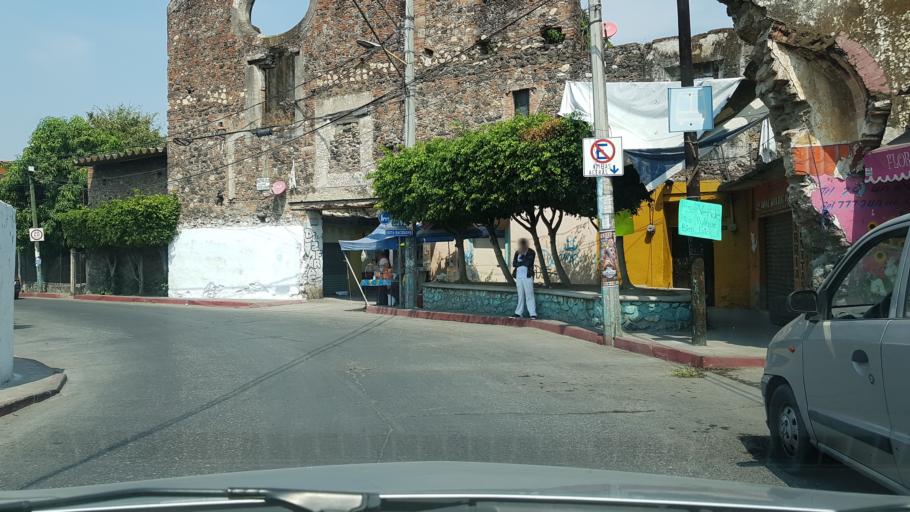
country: MX
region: Morelos
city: Emiliano Zapata
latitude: 18.8381
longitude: -99.1841
